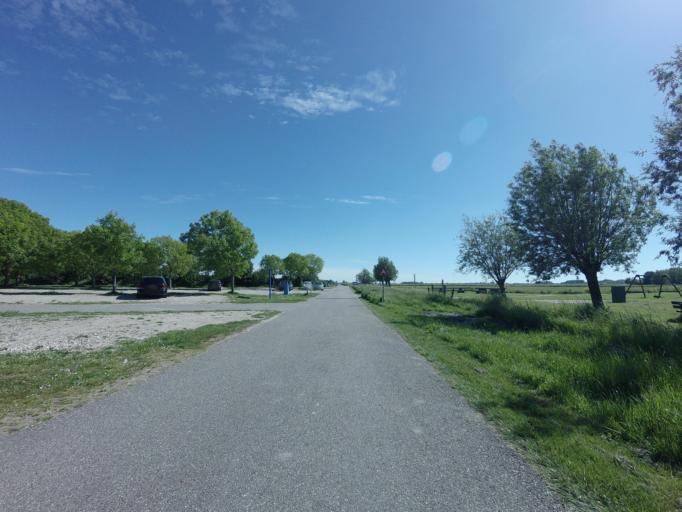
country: NL
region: North Holland
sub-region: Gemeente Uitgeest
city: Uitgeest
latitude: 52.5276
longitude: 4.7335
